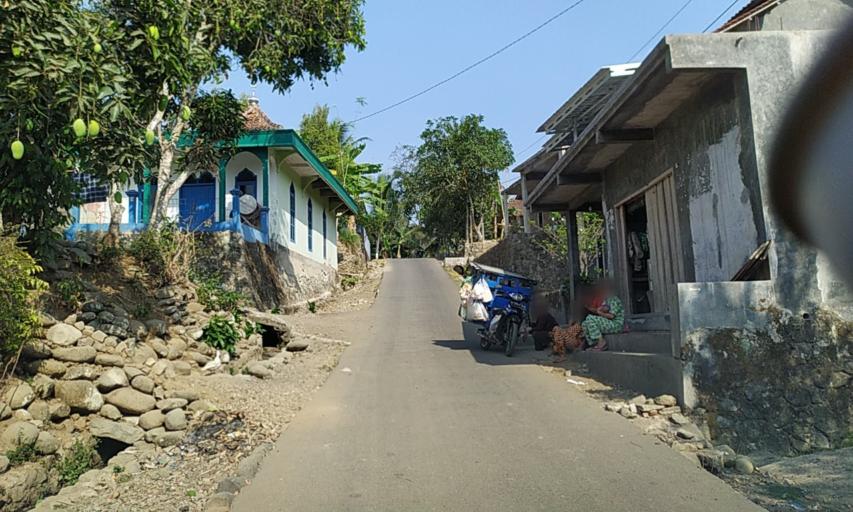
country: ID
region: Central Java
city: Jambuluwuk
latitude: -7.3133
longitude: 108.8691
